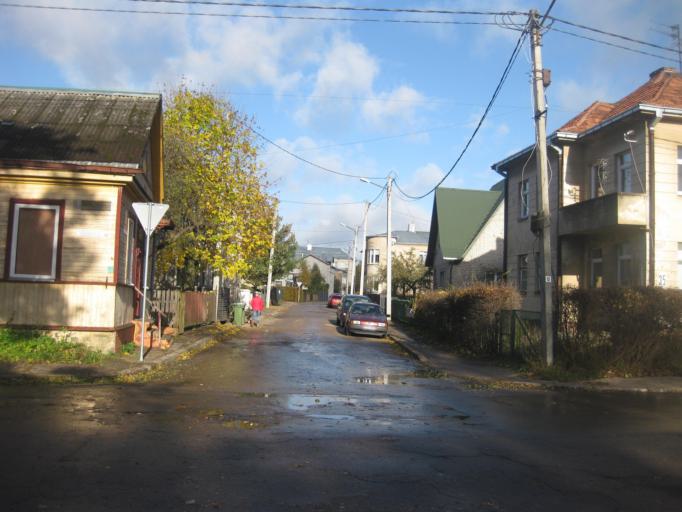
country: LT
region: Kauno apskritis
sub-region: Kaunas
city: Kaunas
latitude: 54.9002
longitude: 23.9299
